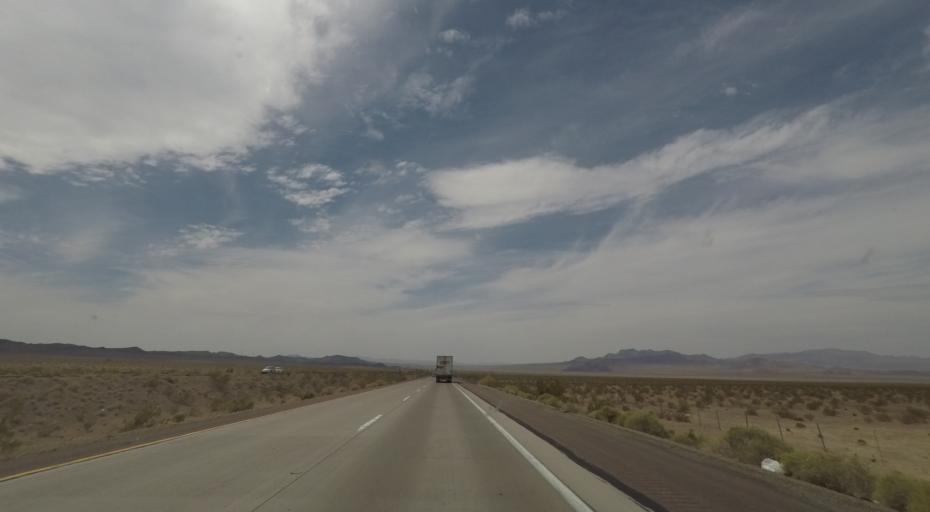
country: US
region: California
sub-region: San Bernardino County
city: Twentynine Palms
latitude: 34.7276
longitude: -116.0990
